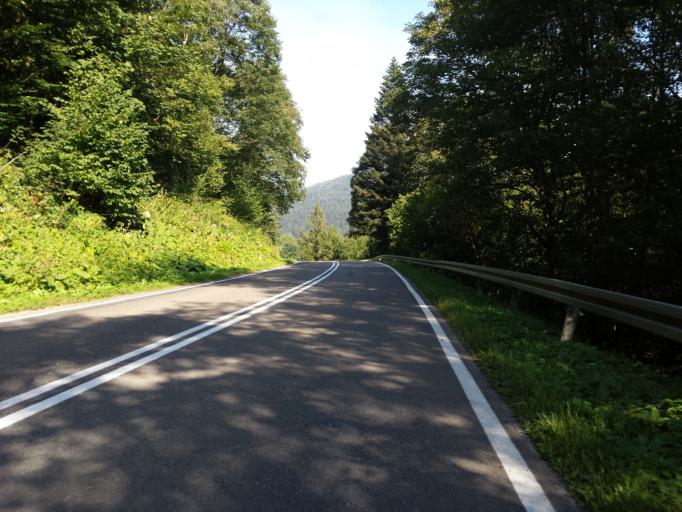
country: PL
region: Subcarpathian Voivodeship
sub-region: Powiat leski
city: Baligrod
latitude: 49.2848
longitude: 22.2758
